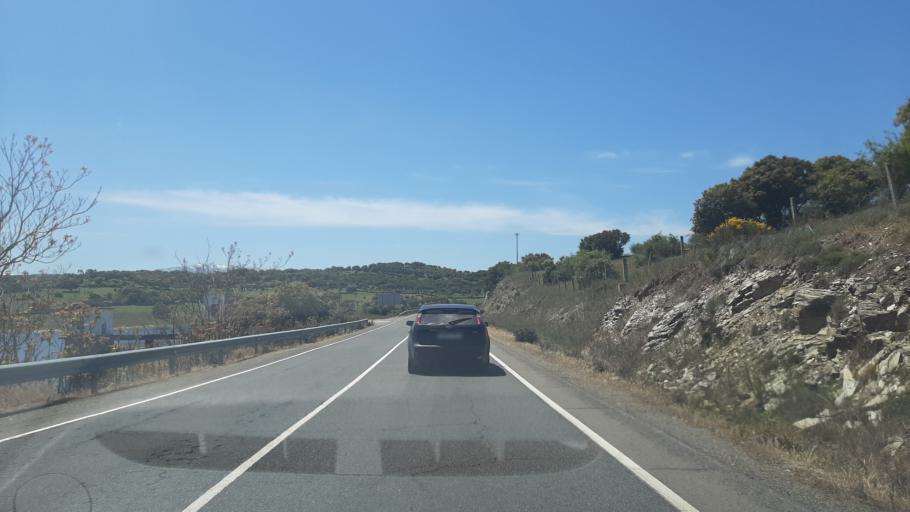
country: ES
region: Castille and Leon
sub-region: Provincia de Salamanca
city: Guijo de Avila
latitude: 40.5520
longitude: -5.6341
